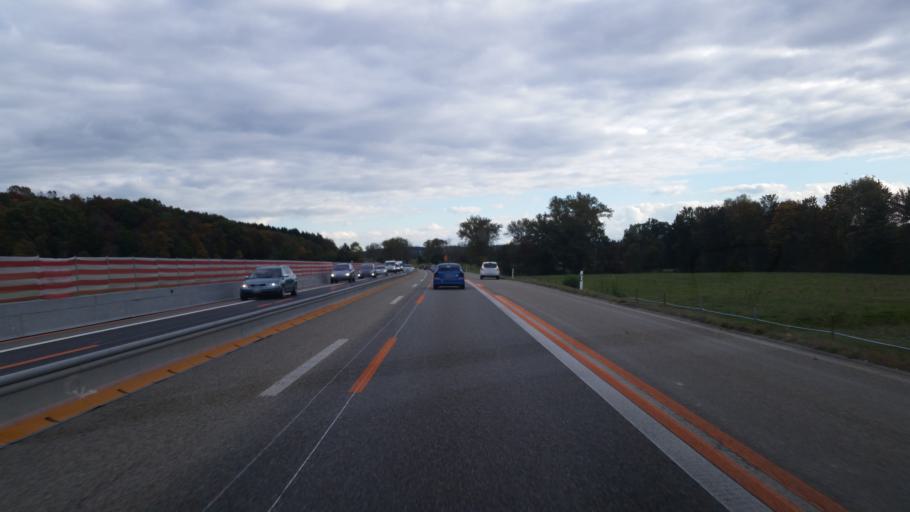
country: CH
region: Zurich
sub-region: Bezirk Buelach
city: Kloten / Freienberg (Chanzler-Chlini Chaseren)
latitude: 47.4732
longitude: 8.5565
